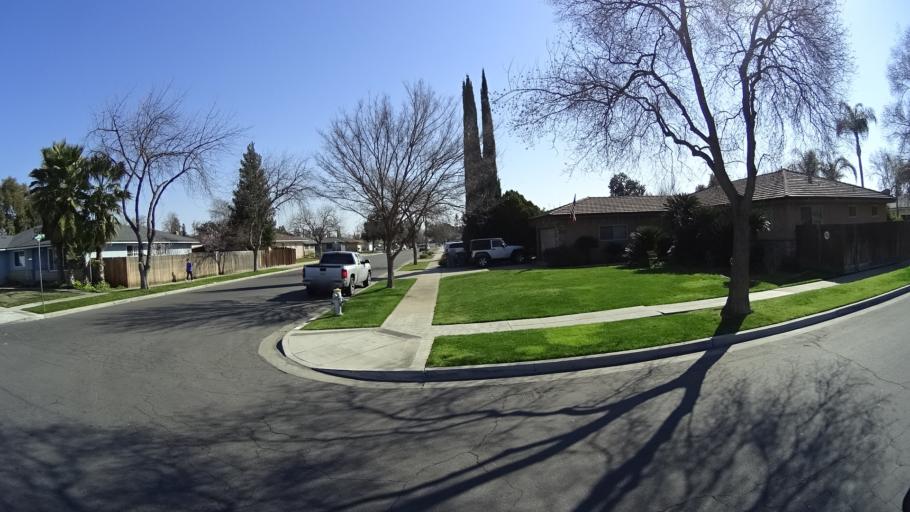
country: US
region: California
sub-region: Fresno County
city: Clovis
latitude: 36.8273
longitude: -119.7763
